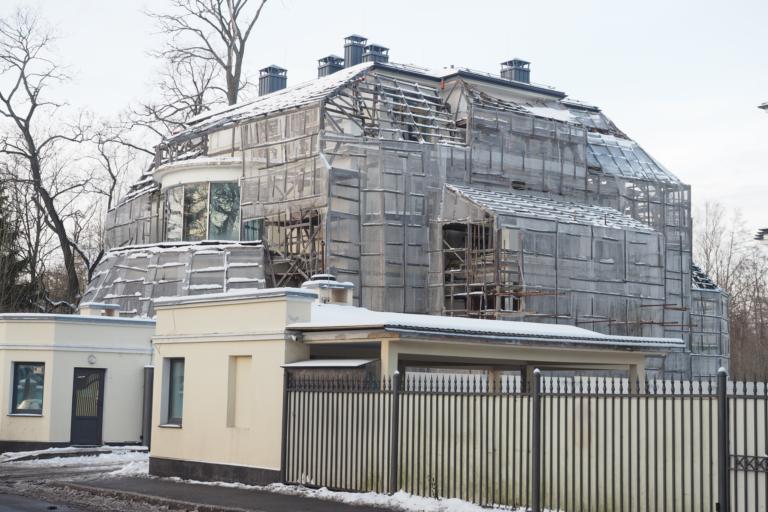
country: RU
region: St.-Petersburg
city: Novaya Derevnya
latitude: 59.9745
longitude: 30.2817
